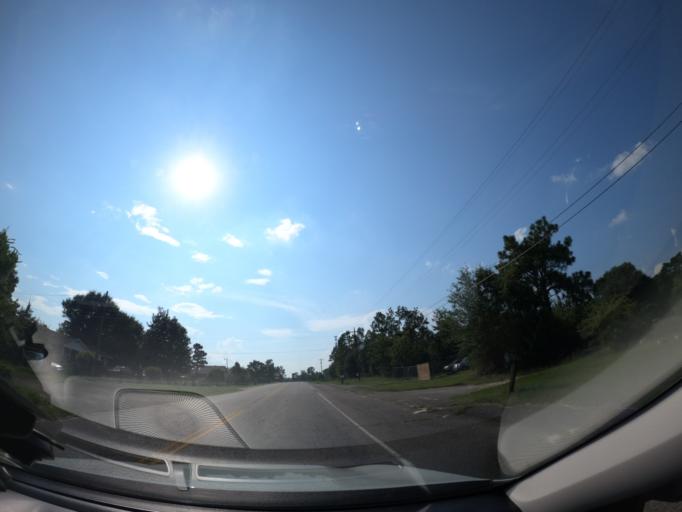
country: US
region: South Carolina
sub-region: Aiken County
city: Jackson
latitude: 33.4104
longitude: -81.7983
